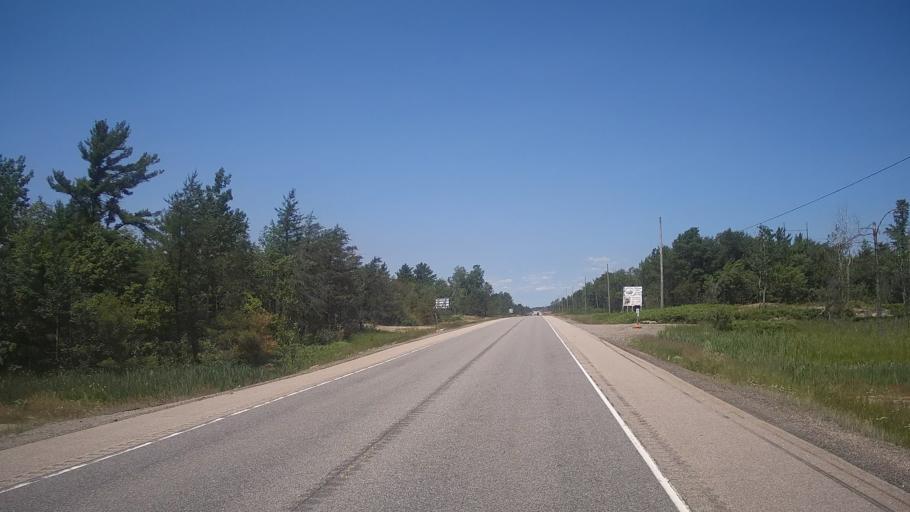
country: CA
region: Ontario
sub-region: Parry Sound District
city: Parry Sound
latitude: 45.7002
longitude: -80.4556
